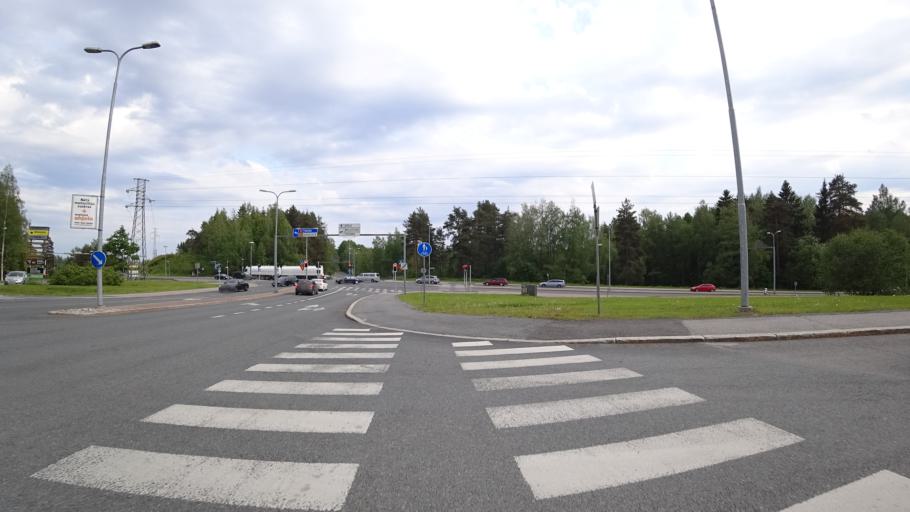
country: FI
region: Pirkanmaa
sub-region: Tampere
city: Pirkkala
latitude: 61.5196
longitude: 23.6426
